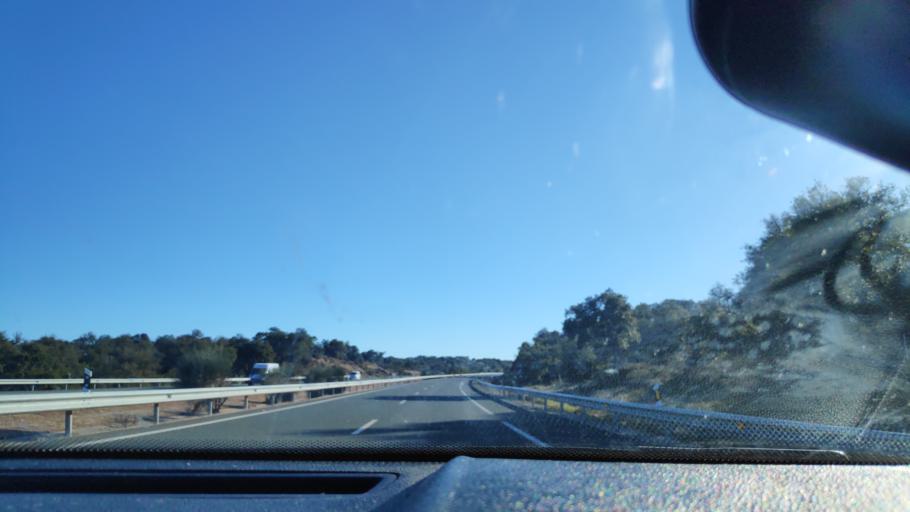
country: ES
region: Andalusia
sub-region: Provincia de Huelva
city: Santa Olalla del Cala
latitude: 37.9385
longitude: -6.2267
